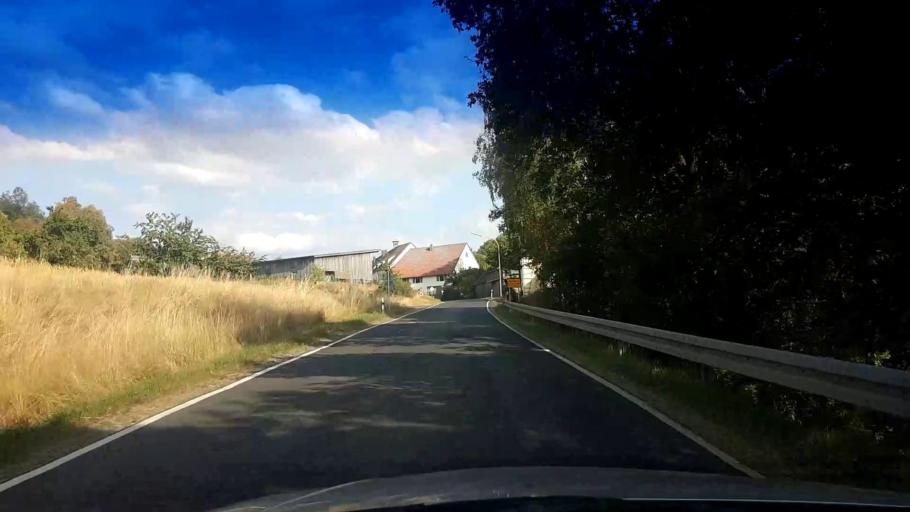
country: DE
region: Bavaria
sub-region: Upper Palatinate
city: Neualbenreuth
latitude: 49.9869
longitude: 12.4148
